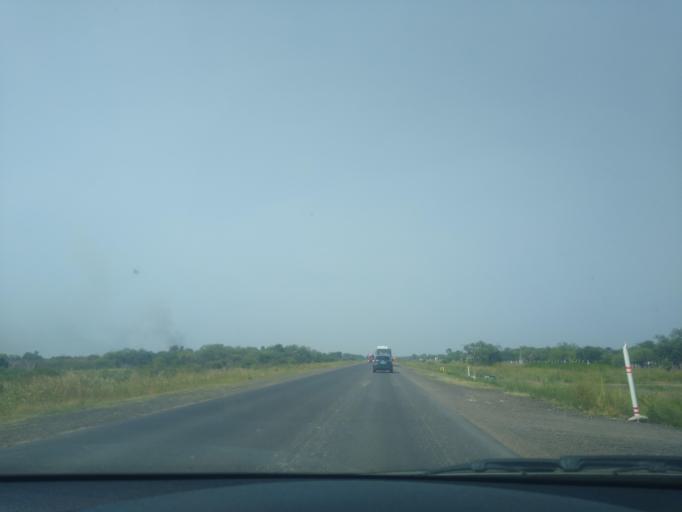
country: AR
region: Chaco
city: Fontana
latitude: -27.4877
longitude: -59.0700
